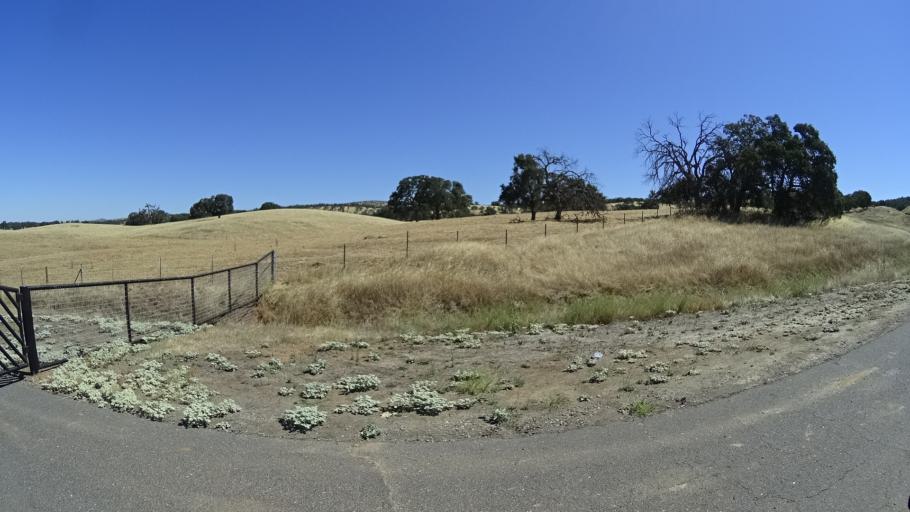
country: US
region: California
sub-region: Calaveras County
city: Copperopolis
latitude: 37.9405
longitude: -120.7543
